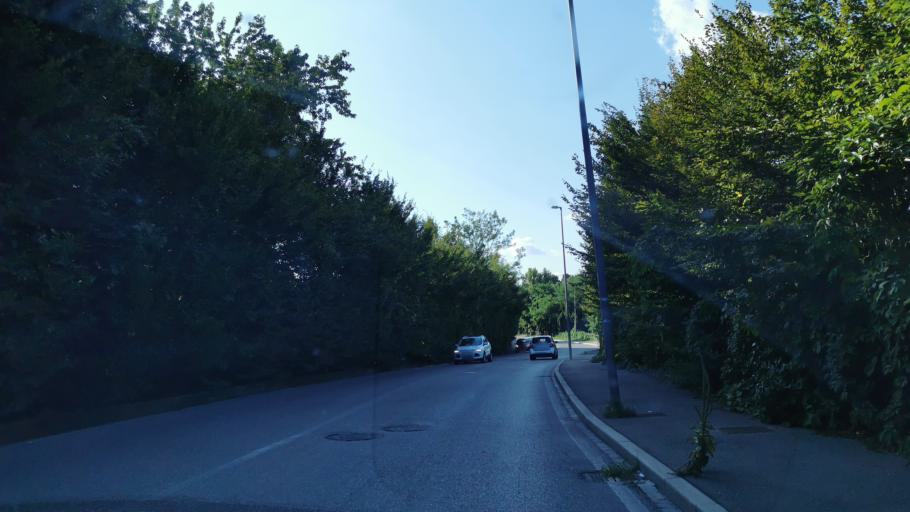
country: IT
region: Lombardy
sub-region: Provincia di Como
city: Grandate
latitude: 45.7797
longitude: 9.0631
